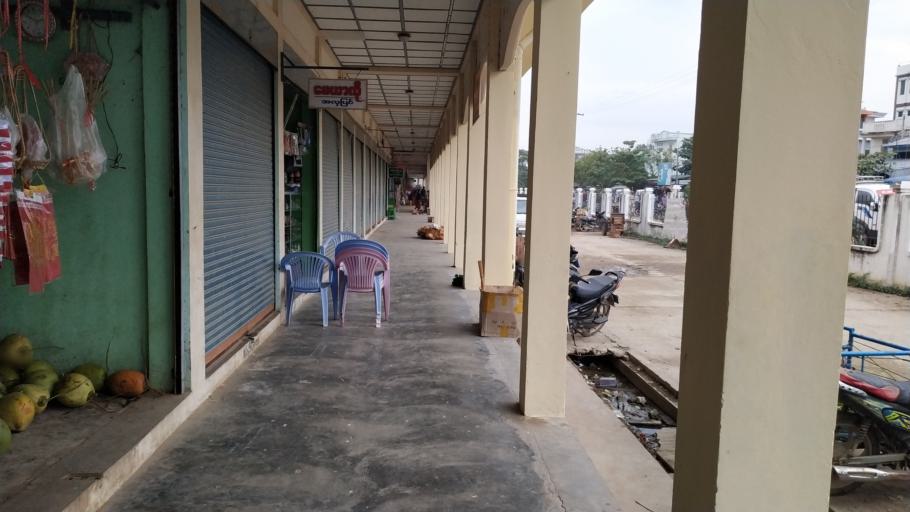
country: MM
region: Mandalay
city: Kyaukse
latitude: 21.5986
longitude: 96.1356
